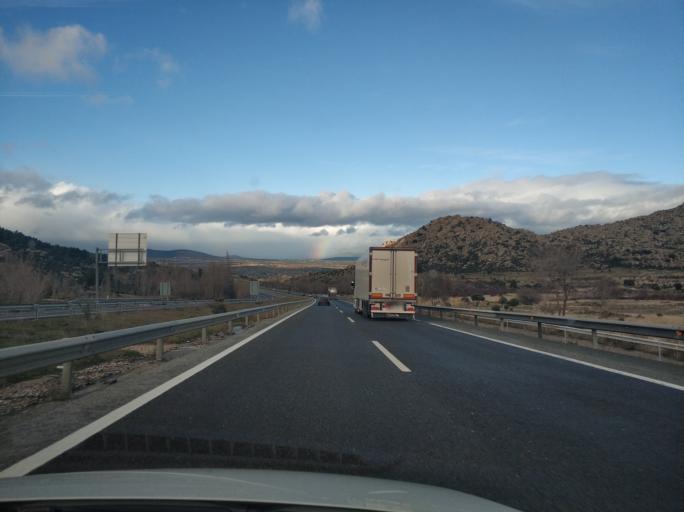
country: ES
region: Madrid
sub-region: Provincia de Madrid
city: La Cabrera
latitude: 40.8819
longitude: -3.5987
